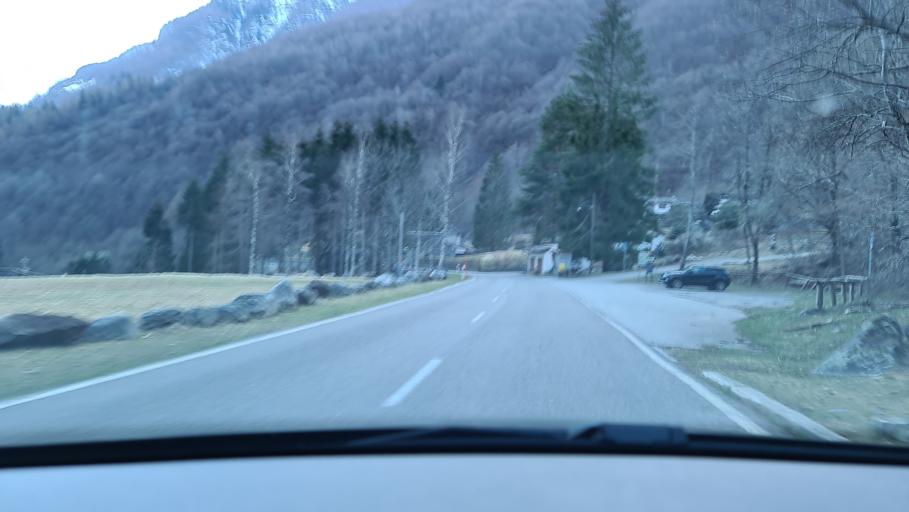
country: CH
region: Ticino
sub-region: Locarno District
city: Lavertezzo
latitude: 46.3305
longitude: 8.8038
